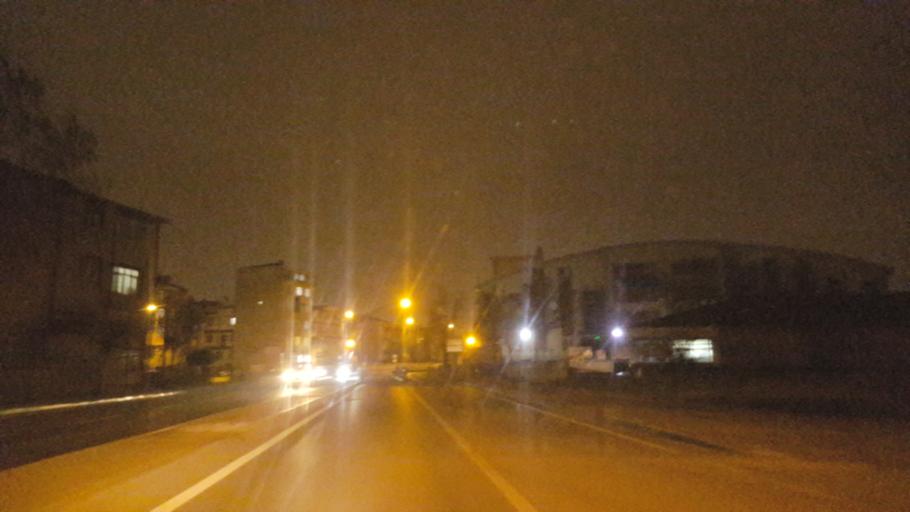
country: TR
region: Kocaeli
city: Darica
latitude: 40.7850
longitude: 29.3994
